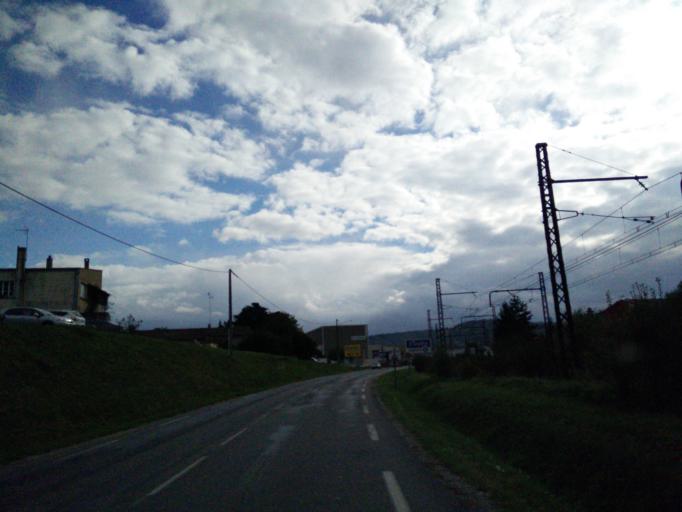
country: FR
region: Midi-Pyrenees
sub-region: Departement du Lot
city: Cahors
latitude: 44.4736
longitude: 1.4285
